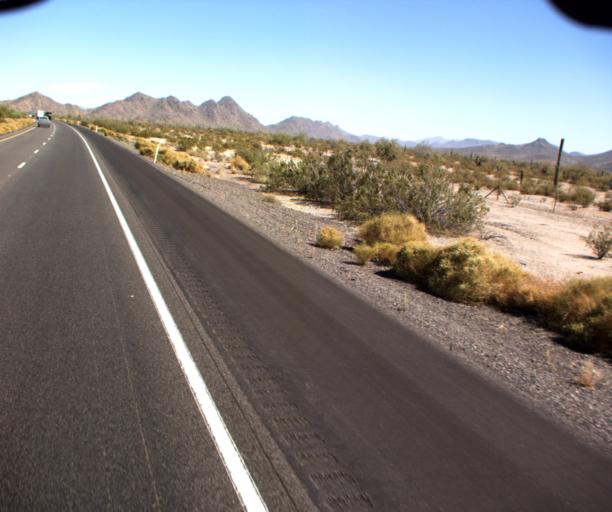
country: US
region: Arizona
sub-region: Maricopa County
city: Gila Bend
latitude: 32.9059
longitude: -112.5829
